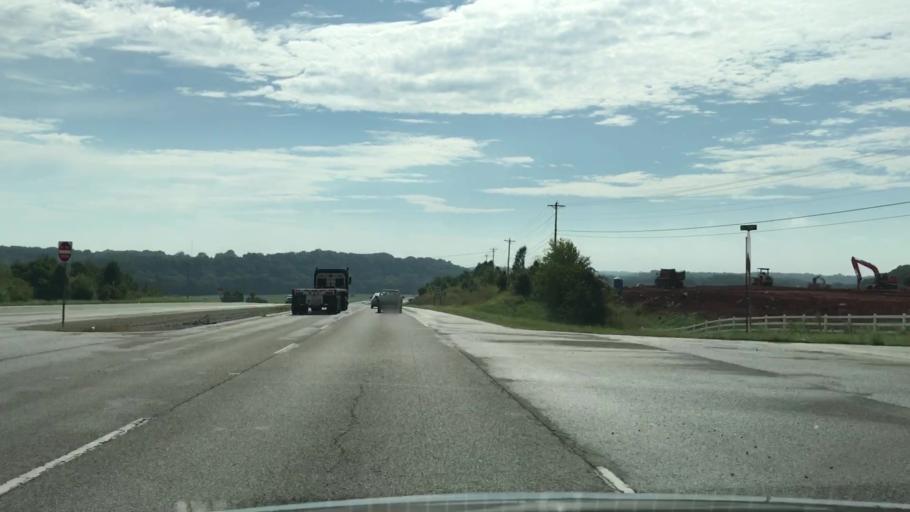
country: US
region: Kentucky
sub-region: Warren County
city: Plano
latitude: 36.9022
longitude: -86.3945
